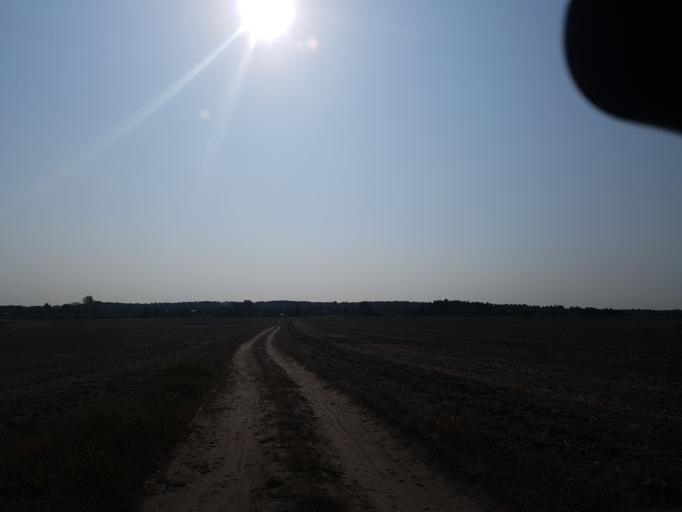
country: DE
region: Brandenburg
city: Wiesenburg
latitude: 52.0606
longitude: 12.3743
